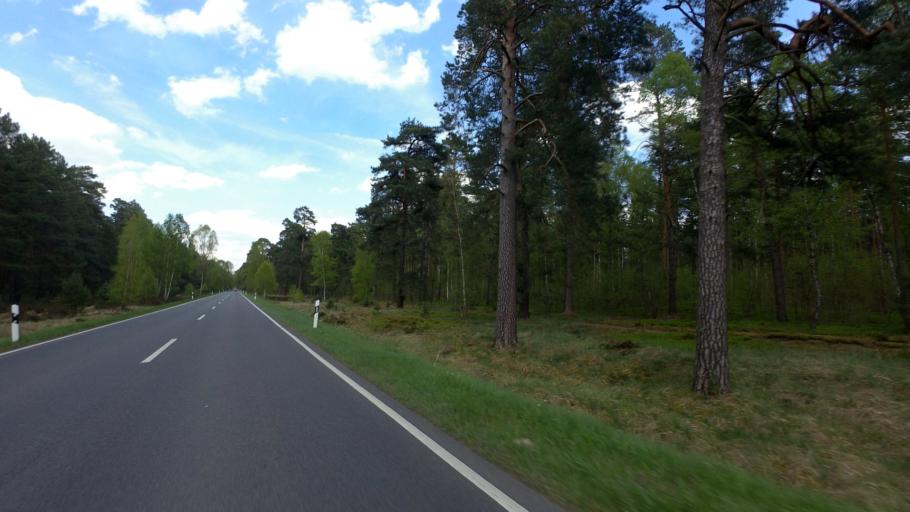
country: DE
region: Brandenburg
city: Marienwerder
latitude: 52.9700
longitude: 13.5757
